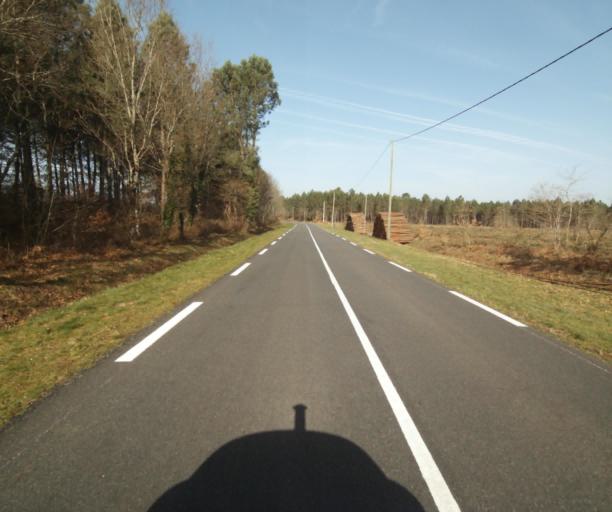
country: FR
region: Aquitaine
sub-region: Departement de la Gironde
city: Grignols
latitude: 44.2071
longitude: -0.1548
